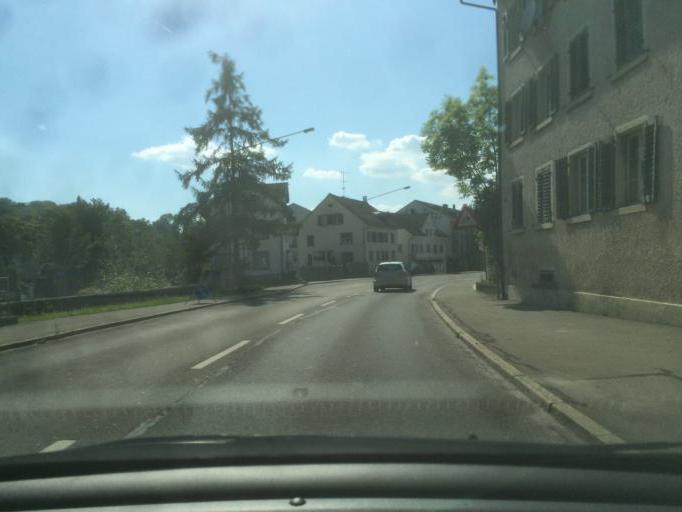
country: CH
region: Zurich
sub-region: Bezirk Uster
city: Uster / Ober-Uster
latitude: 47.3450
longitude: 8.7326
